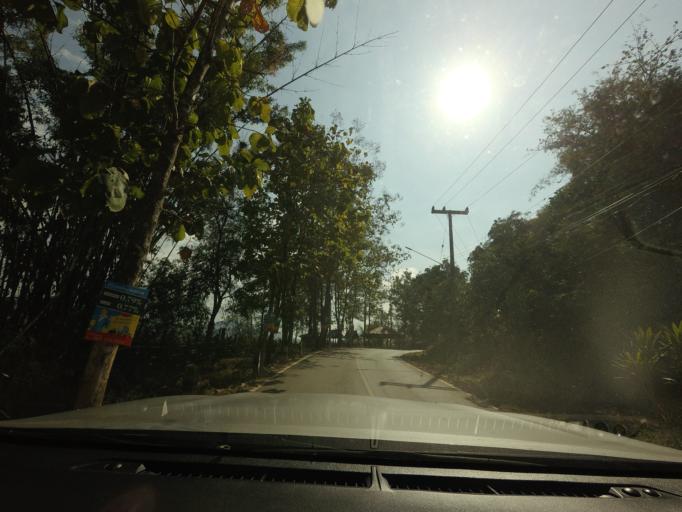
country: TH
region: Mae Hong Son
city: Wiang Nuea
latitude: 19.3999
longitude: 98.4428
